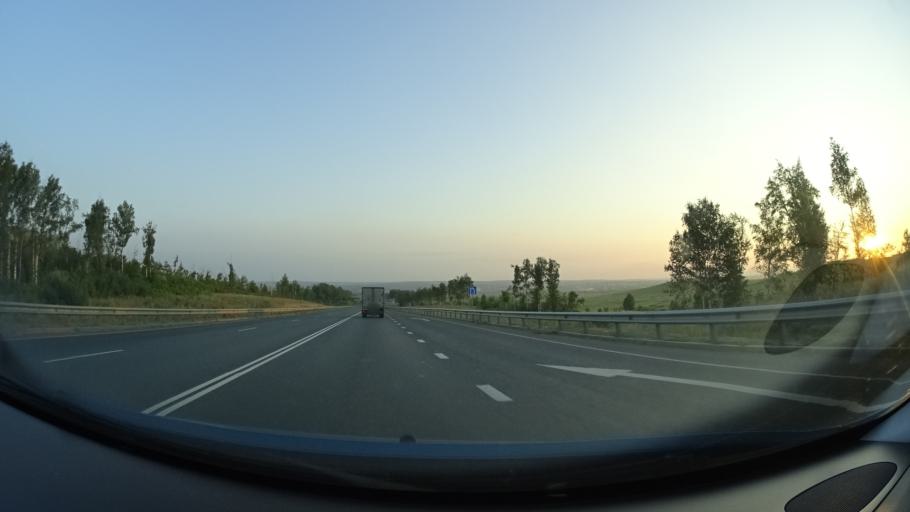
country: RU
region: Samara
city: Sernovodsk
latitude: 53.9097
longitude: 51.2938
